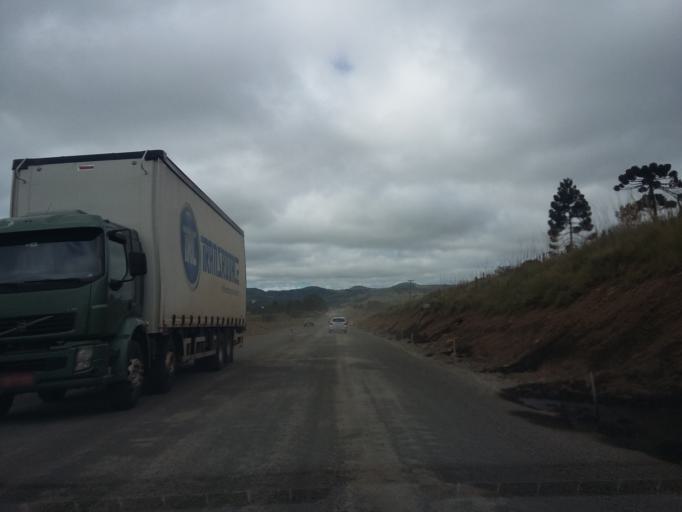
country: BR
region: Santa Catarina
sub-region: Lages
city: Lages
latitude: -27.9077
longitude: -50.1167
